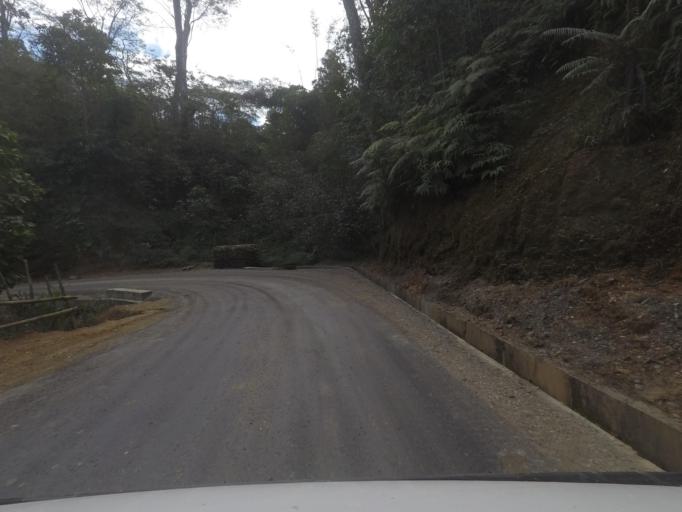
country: TL
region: Ermera
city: Gleno
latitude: -8.7460
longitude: 125.3467
